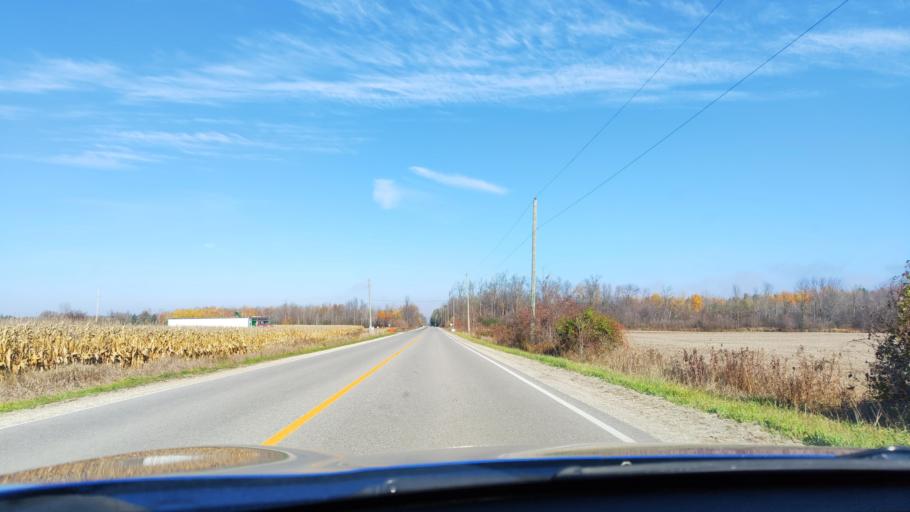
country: CA
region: Ontario
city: Wasaga Beach
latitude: 44.4010
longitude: -80.0580
